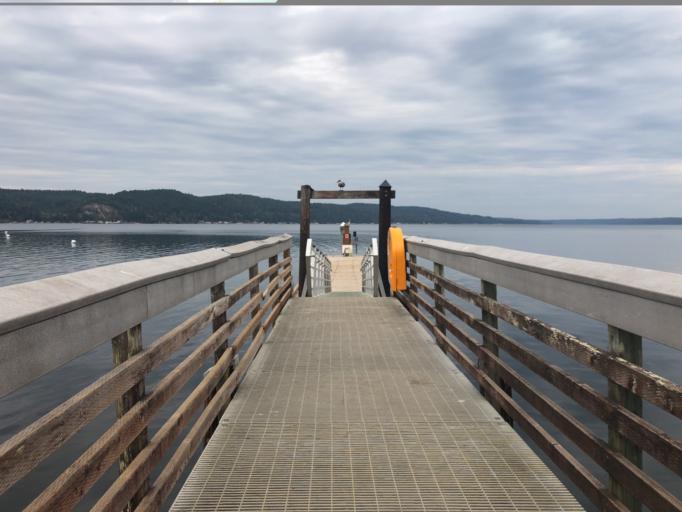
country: US
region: Washington
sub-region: Mason County
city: Allyn
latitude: 47.3787
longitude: -122.9702
